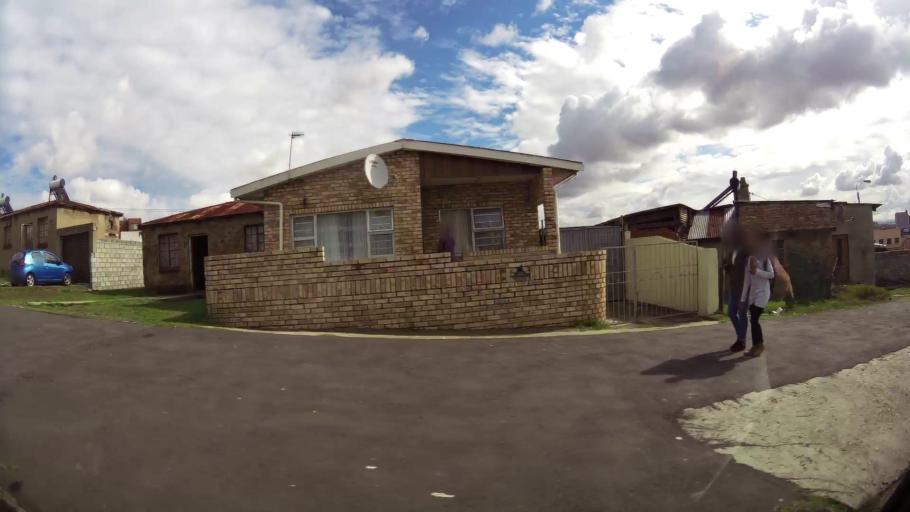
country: ZA
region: Eastern Cape
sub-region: Nelson Mandela Bay Metropolitan Municipality
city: Port Elizabeth
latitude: -33.9334
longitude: 25.5757
